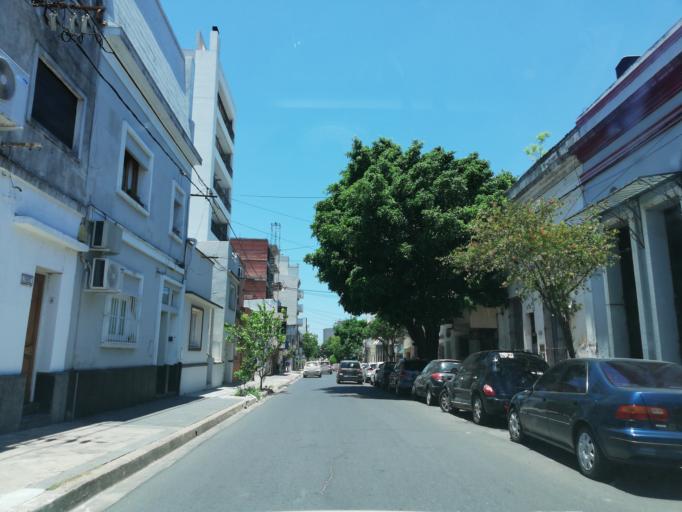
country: AR
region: Corrientes
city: Corrientes
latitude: -27.4649
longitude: -58.8301
